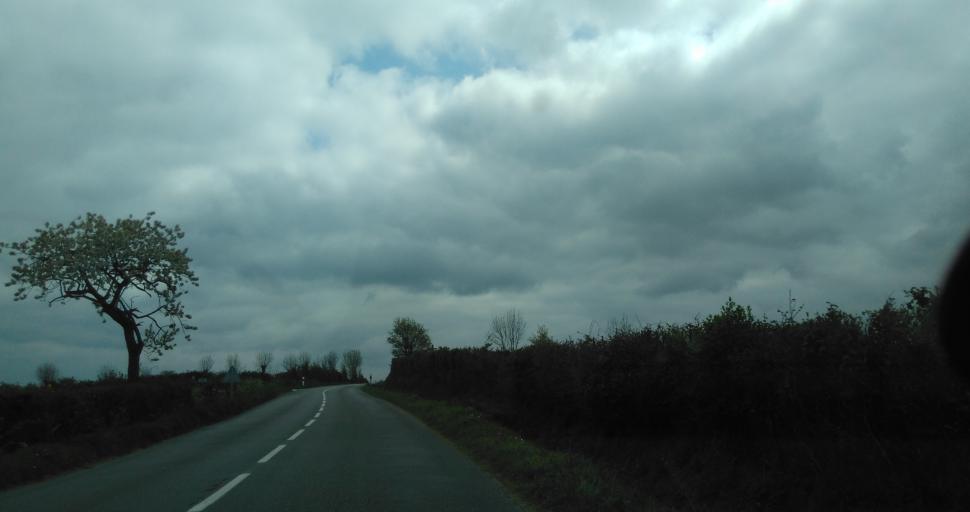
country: FR
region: Poitou-Charentes
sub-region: Departement des Deux-Sevres
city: Moncoutant
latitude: 46.7218
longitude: -0.5627
